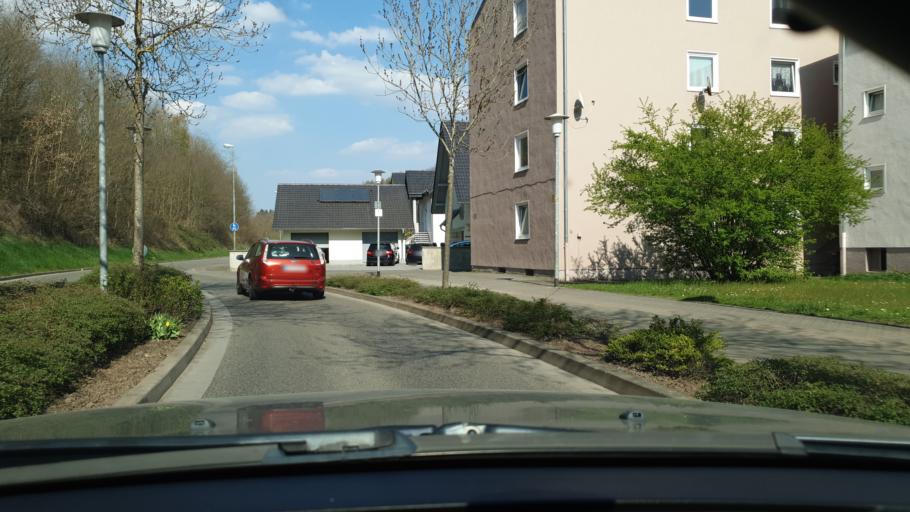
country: DE
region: Rheinland-Pfalz
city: Zweibrucken
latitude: 49.2601
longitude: 7.3989
